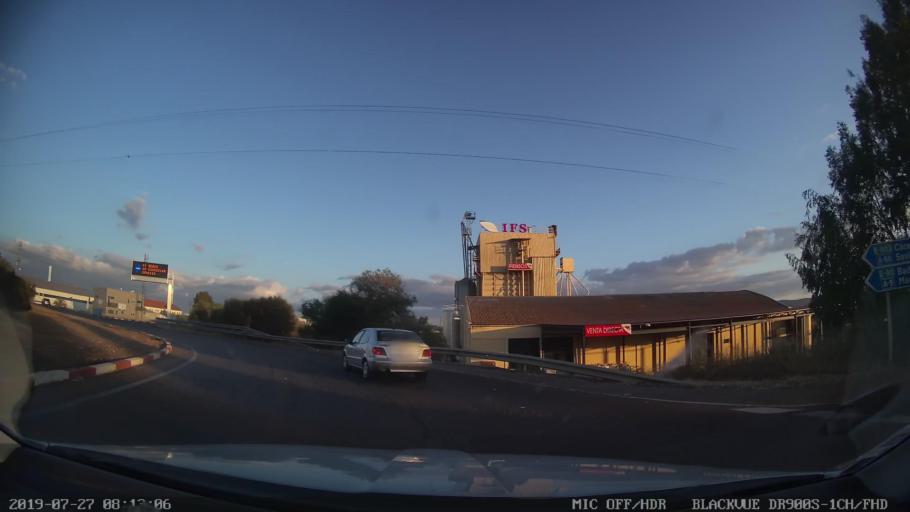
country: ES
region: Extremadura
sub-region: Provincia de Badajoz
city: Calamonte
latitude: 38.9052
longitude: -6.3682
